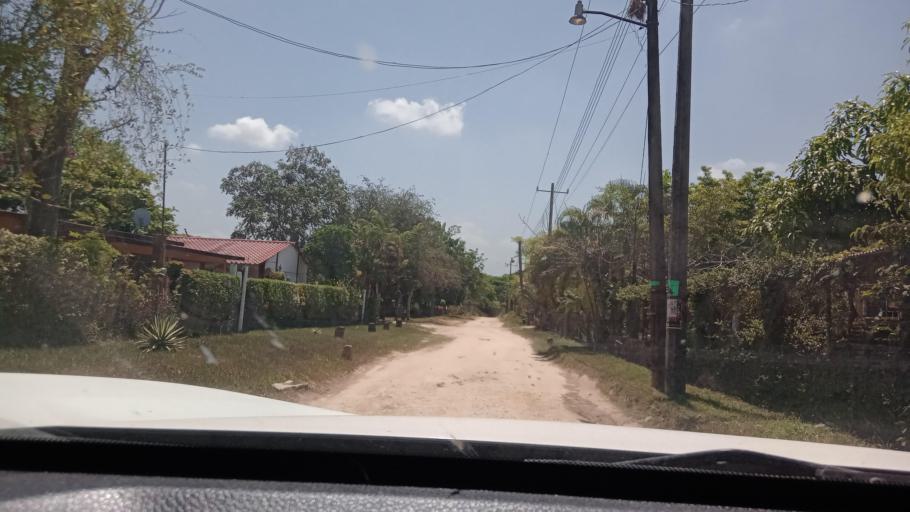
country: MX
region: Veracruz
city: Las Choapas
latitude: 17.7541
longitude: -94.1110
